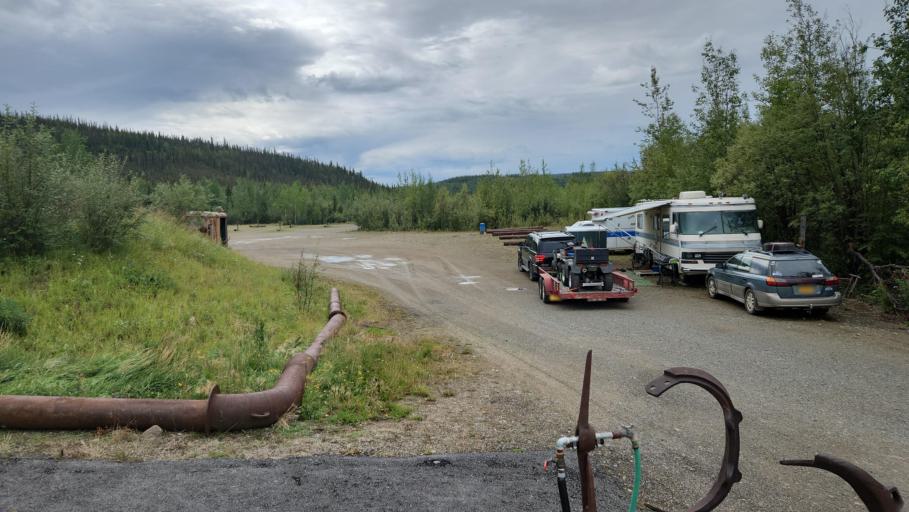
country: US
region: Alaska
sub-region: Southeast Fairbanks Census Area
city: Tok
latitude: 64.0718
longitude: -141.9346
